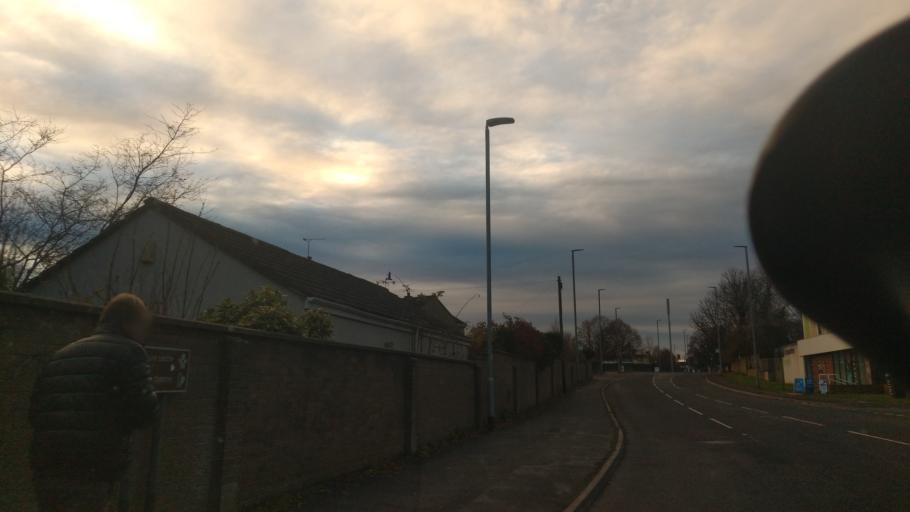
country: GB
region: England
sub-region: Somerset
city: Frome
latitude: 51.2378
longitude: -2.3137
